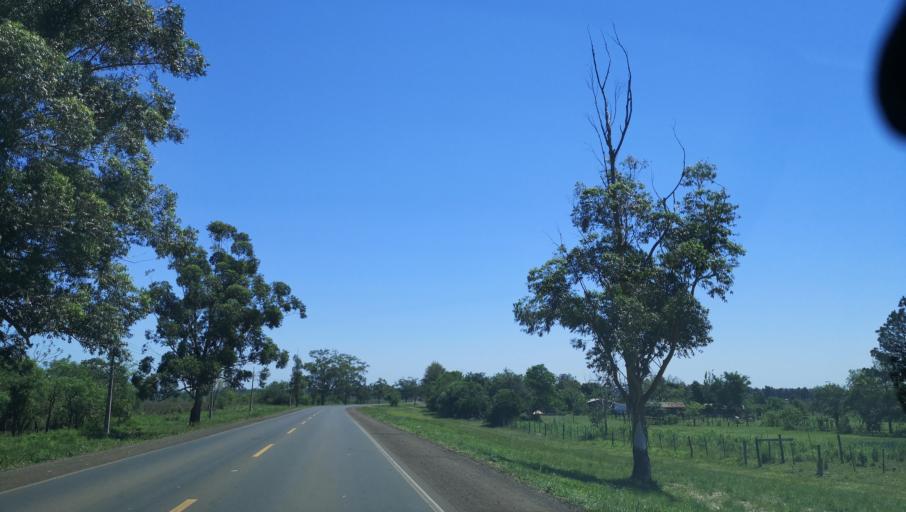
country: PY
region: Itapua
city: Carmen del Parana
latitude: -27.2215
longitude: -56.1170
